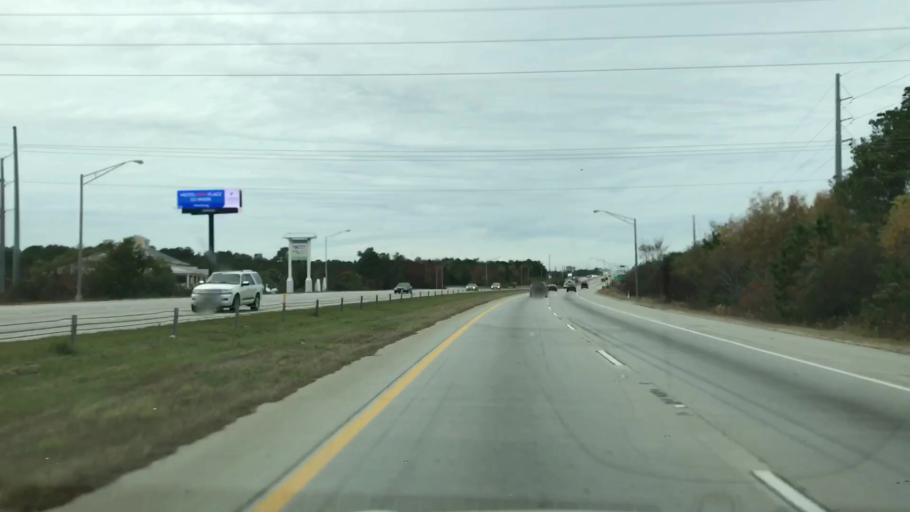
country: US
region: South Carolina
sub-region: Charleston County
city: North Charleston
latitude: 32.8752
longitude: -79.9260
